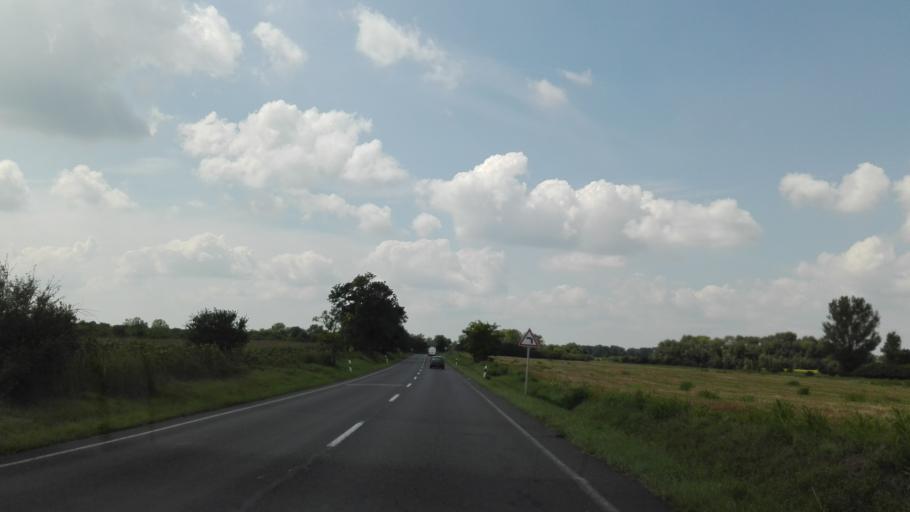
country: HU
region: Fejer
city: Alap
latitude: 46.7991
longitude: 18.7239
